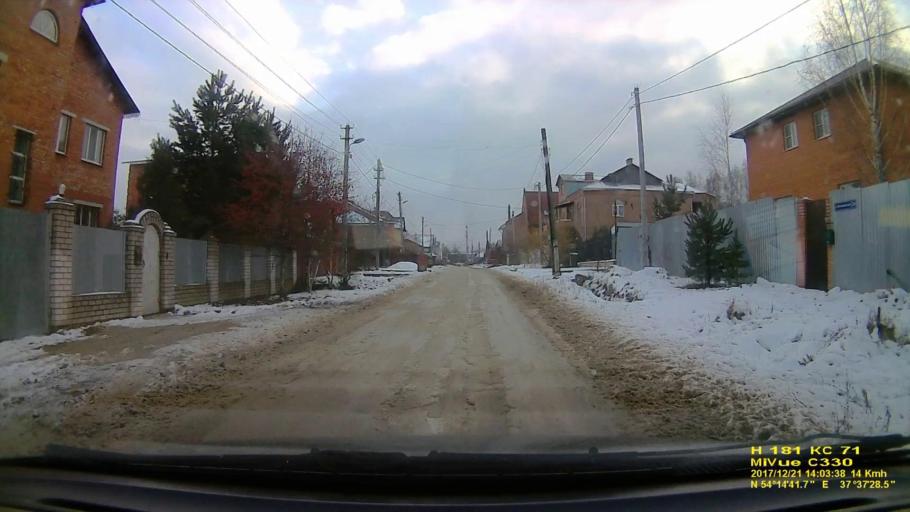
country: RU
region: Tula
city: Gorelki
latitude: 54.2449
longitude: 37.6246
